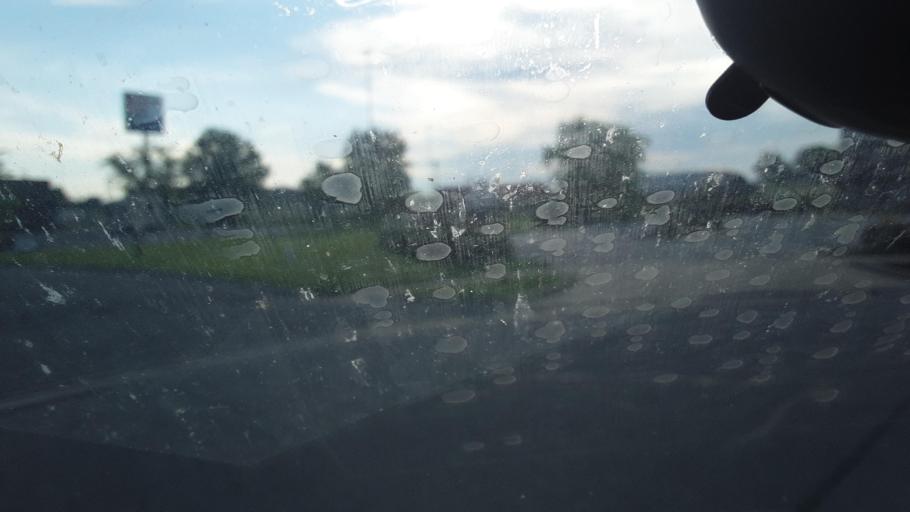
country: US
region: Indiana
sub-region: DeKalb County
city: Auburn
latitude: 41.3653
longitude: -85.0845
